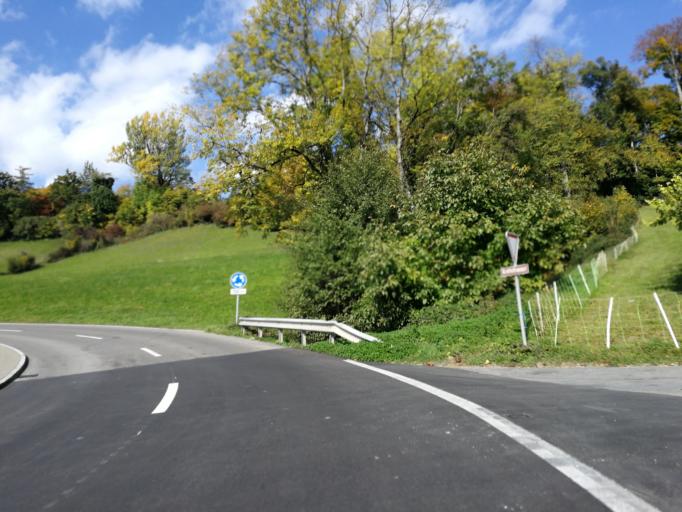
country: CH
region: Zurich
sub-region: Bezirk Meilen
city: Uetikon / Grossdorf
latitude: 47.2710
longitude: 8.6724
